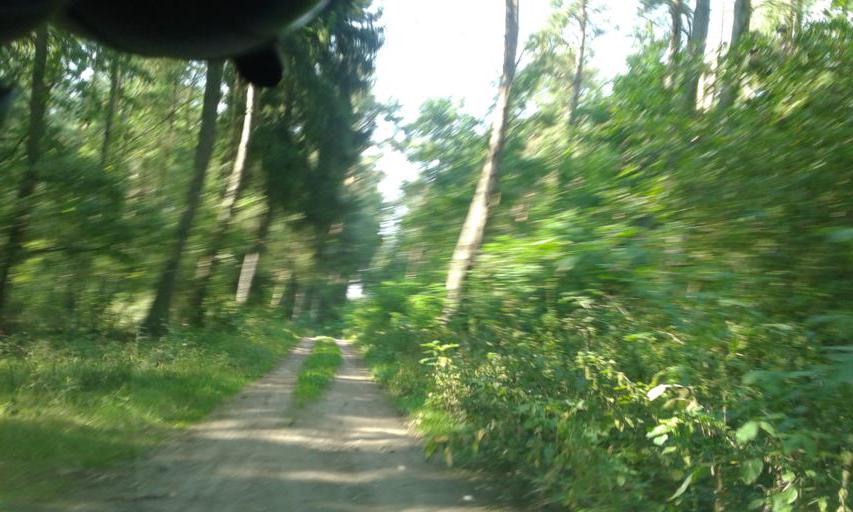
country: PL
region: West Pomeranian Voivodeship
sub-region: Powiat choszczenski
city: Krzecin
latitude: 53.0941
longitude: 15.4383
